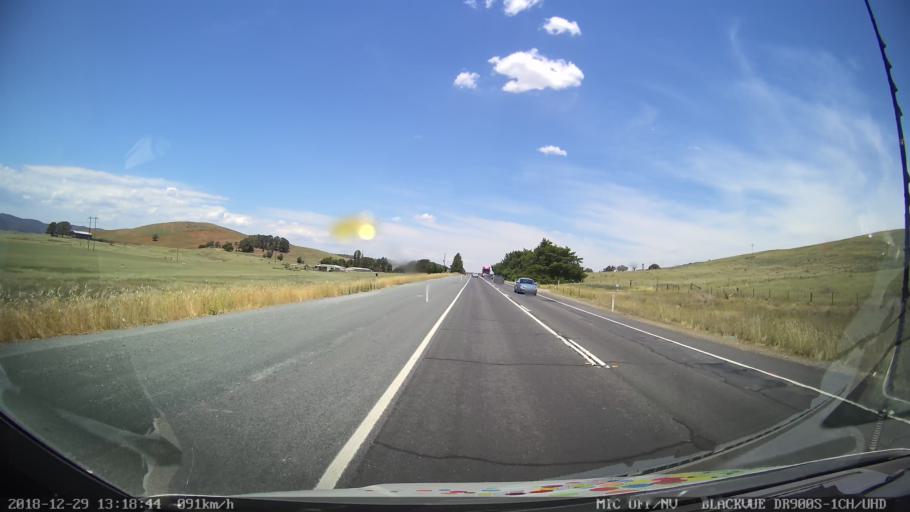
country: AU
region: Australian Capital Territory
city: Macarthur
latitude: -35.7554
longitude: 149.1610
